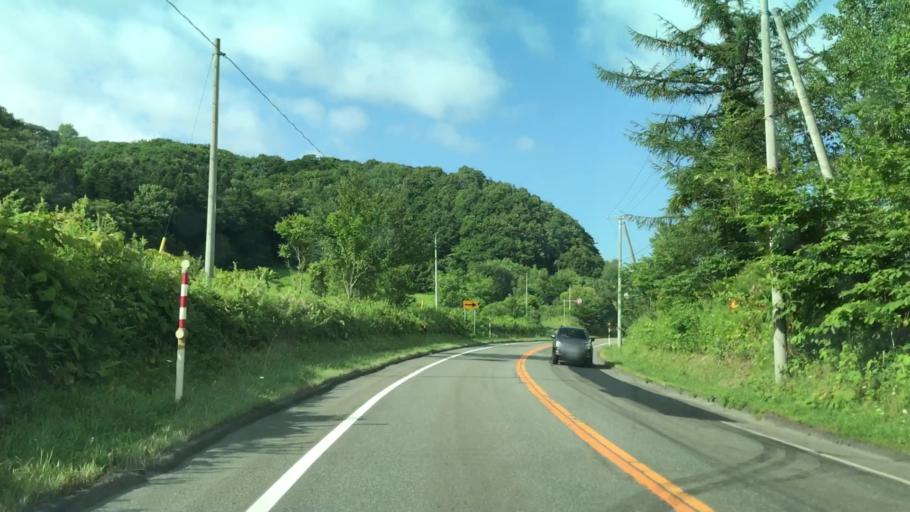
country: JP
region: Hokkaido
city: Shizunai-furukawacho
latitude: 42.7975
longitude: 142.3954
